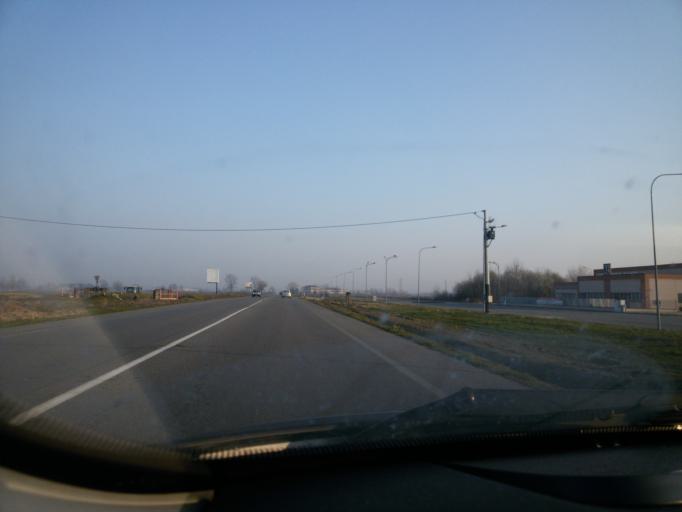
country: IT
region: Piedmont
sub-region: Provincia di Vercelli
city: Pezzana
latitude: 45.2614
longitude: 8.4640
